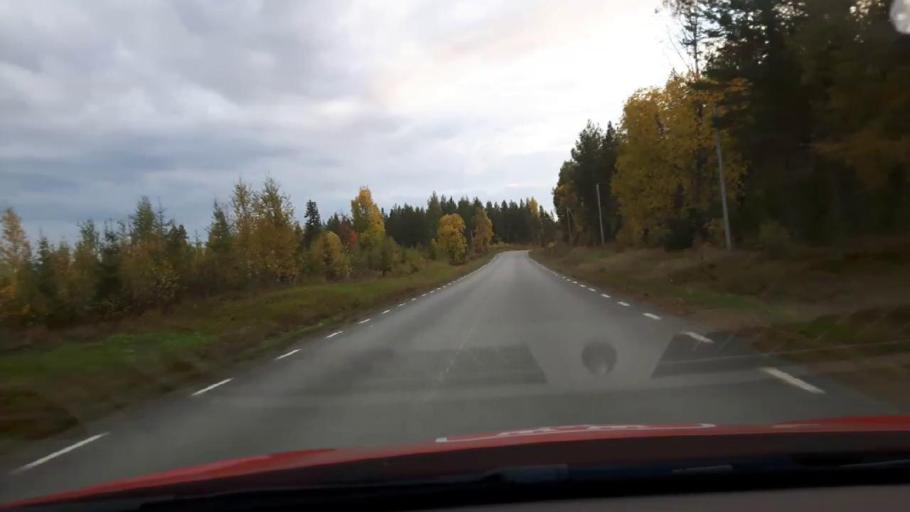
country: SE
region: Jaemtland
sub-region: OEstersunds Kommun
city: Lit
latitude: 63.3172
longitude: 15.1456
